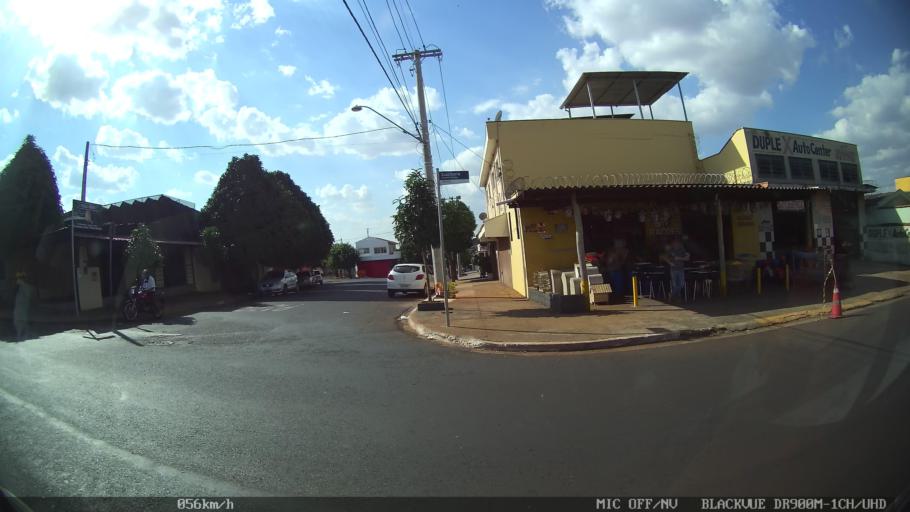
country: BR
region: Sao Paulo
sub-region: Ribeirao Preto
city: Ribeirao Preto
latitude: -21.1993
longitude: -47.8371
